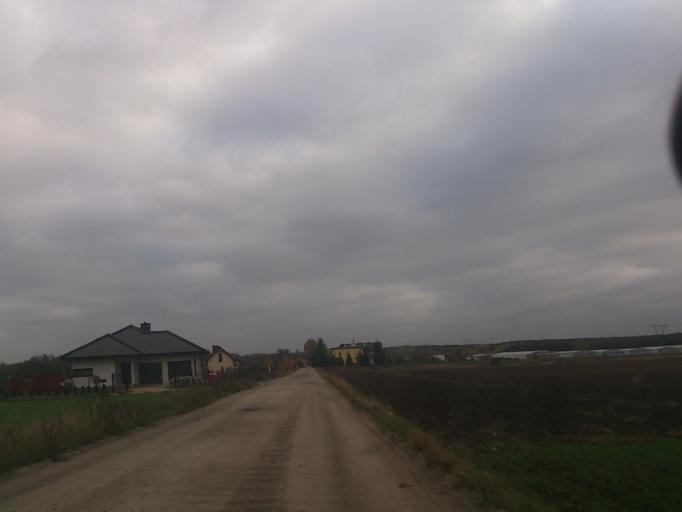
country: PL
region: Kujawsko-Pomorskie
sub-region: Powiat golubsko-dobrzynski
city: Golub-Dobrzyn
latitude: 53.1302
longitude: 19.0930
